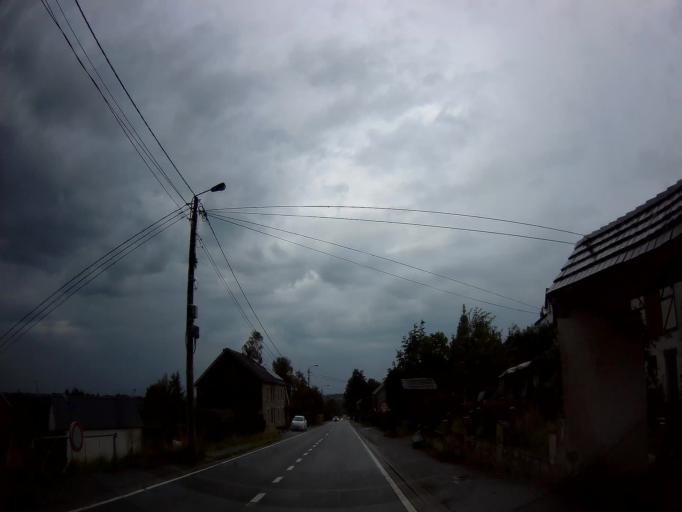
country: BE
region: Wallonia
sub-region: Province de Liege
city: Ferrieres
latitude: 50.4426
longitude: 5.6182
